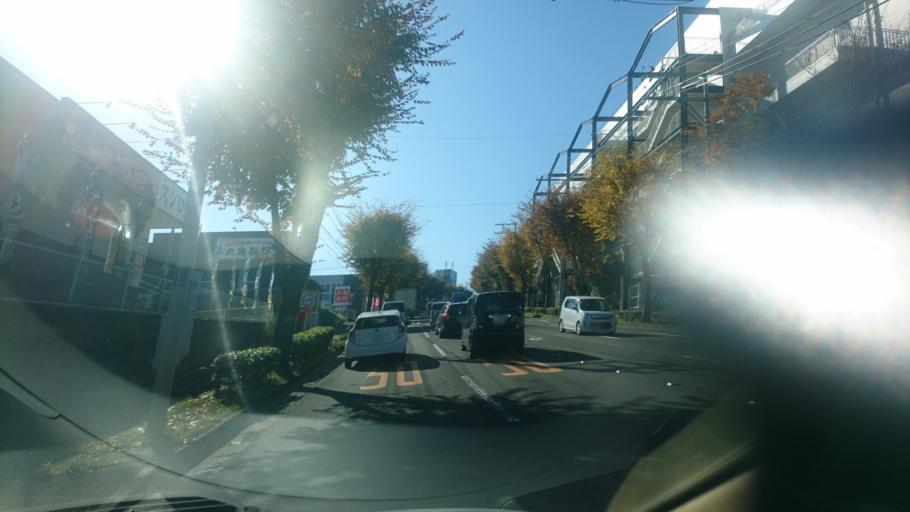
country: JP
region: Miyagi
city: Sendai-shi
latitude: 38.2996
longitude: 140.8296
